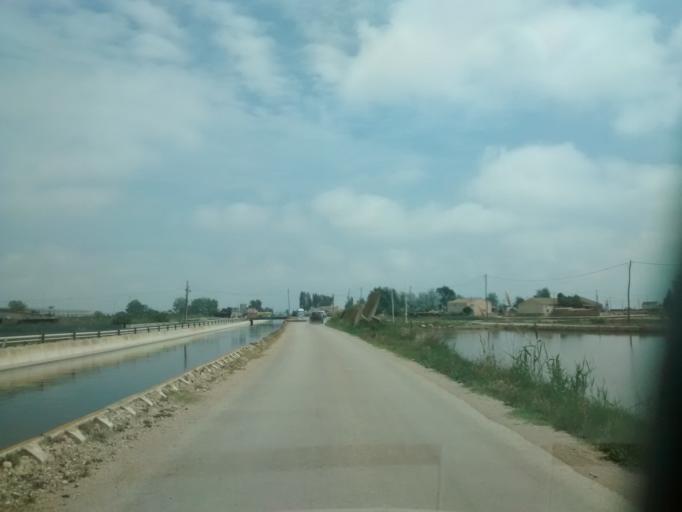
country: ES
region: Catalonia
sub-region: Provincia de Tarragona
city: Deltebre
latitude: 40.7021
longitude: 0.7282
